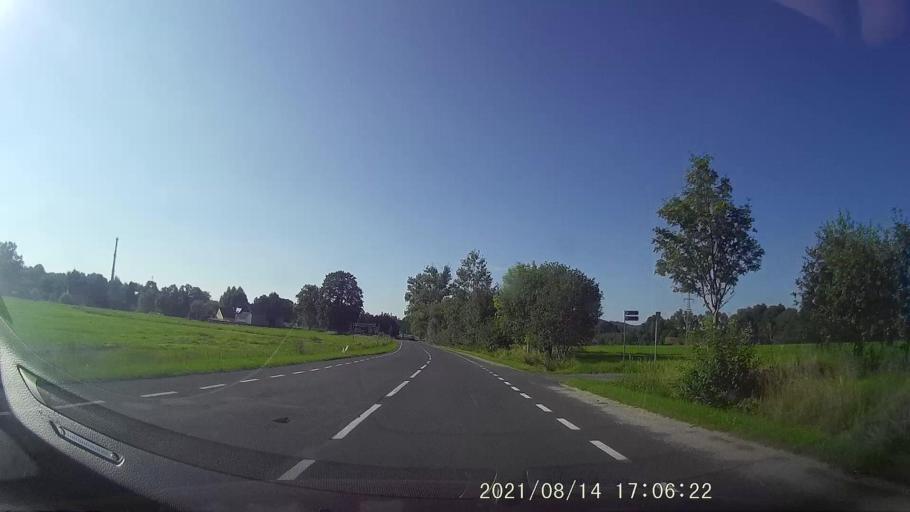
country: PL
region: Lower Silesian Voivodeship
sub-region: Powiat jeleniogorski
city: Kowary
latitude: 50.8099
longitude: 15.8150
